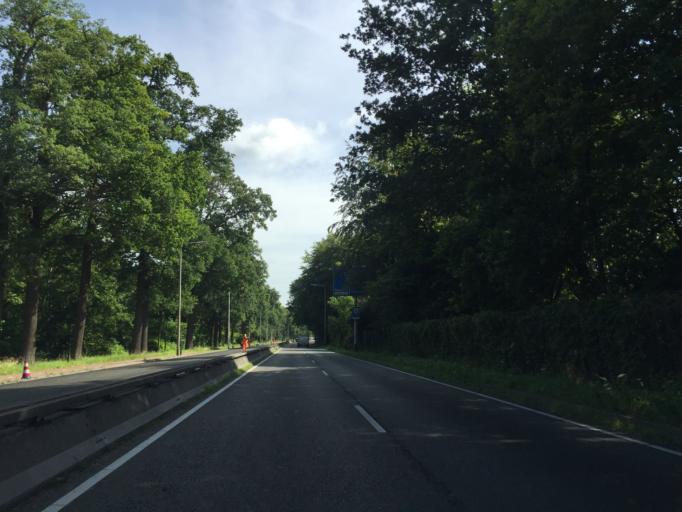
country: NL
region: South Holland
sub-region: Gemeente Wassenaar
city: Wassenaar
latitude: 52.1343
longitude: 4.4012
